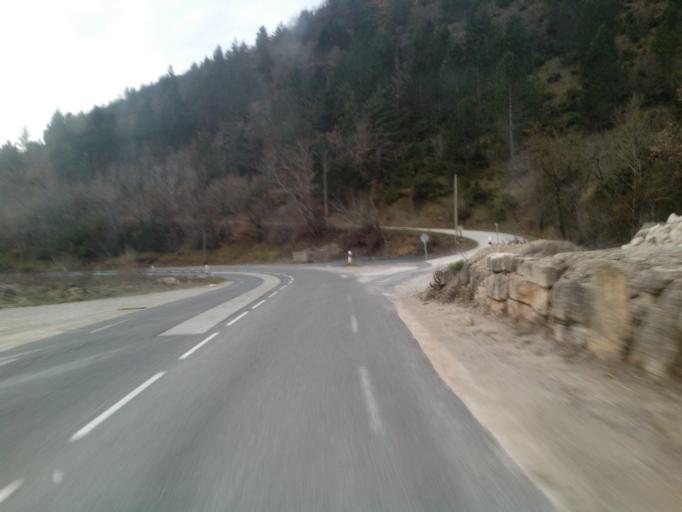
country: FR
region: Languedoc-Roussillon
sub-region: Departement de la Lozere
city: Florac
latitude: 44.2950
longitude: 3.5959
